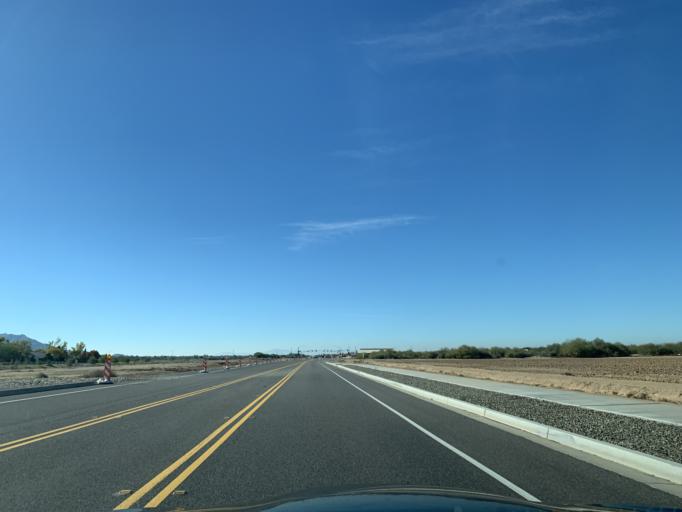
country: US
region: Arizona
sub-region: Maricopa County
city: Queen Creek
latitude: 33.2195
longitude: -111.6289
